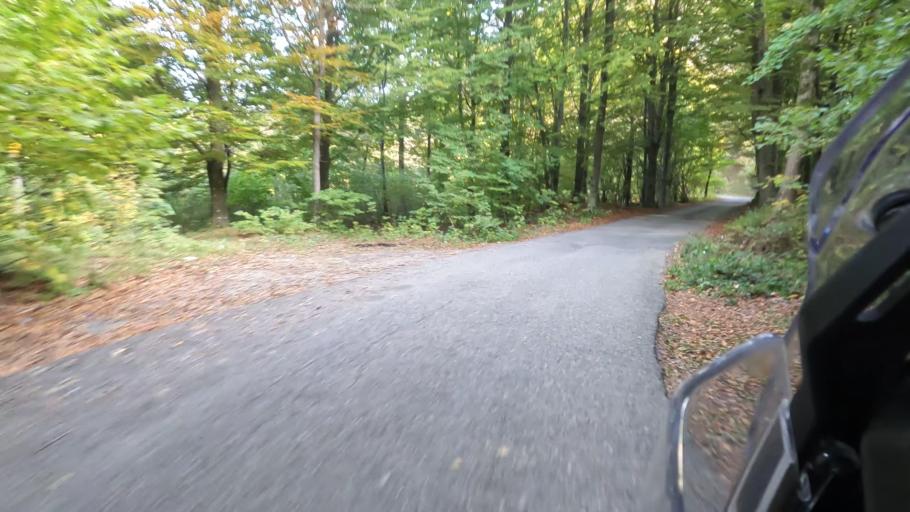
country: IT
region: Liguria
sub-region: Provincia di Savona
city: Urbe
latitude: 44.4393
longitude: 8.5815
